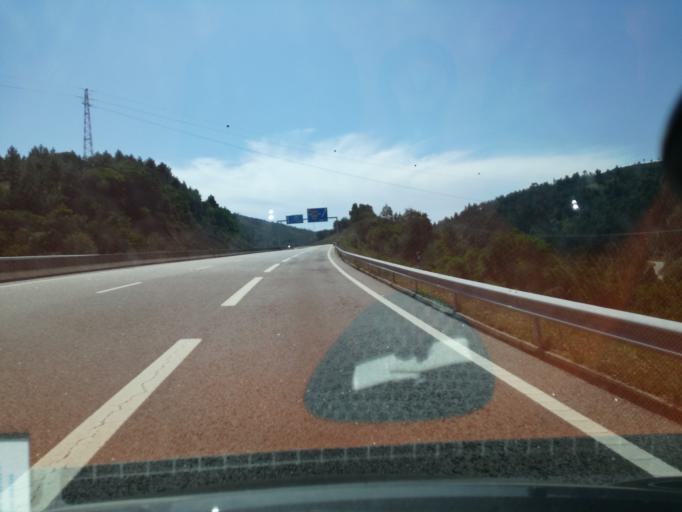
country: PT
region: Viana do Castelo
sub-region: Vila Nova de Cerveira
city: Vila Nova de Cerveira
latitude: 41.8595
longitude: -8.7778
